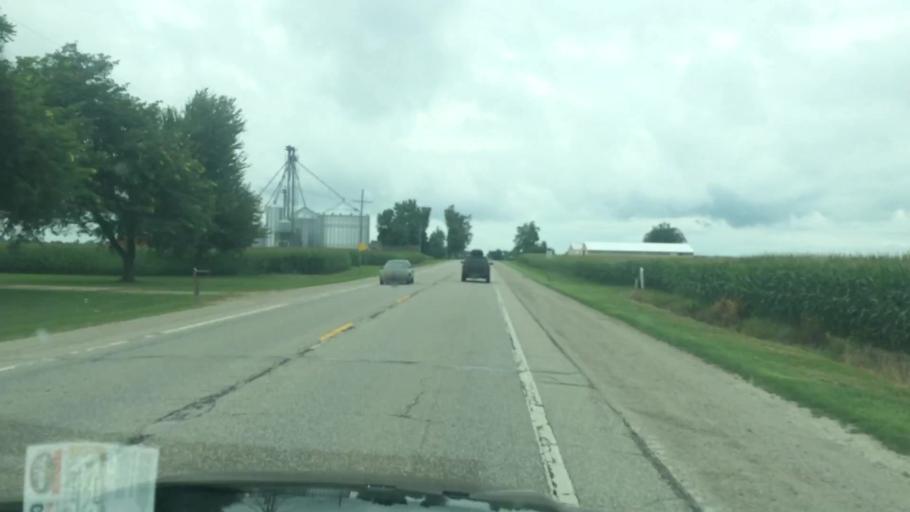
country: US
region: Michigan
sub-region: Sanilac County
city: Marlette
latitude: 43.2726
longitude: -83.0794
